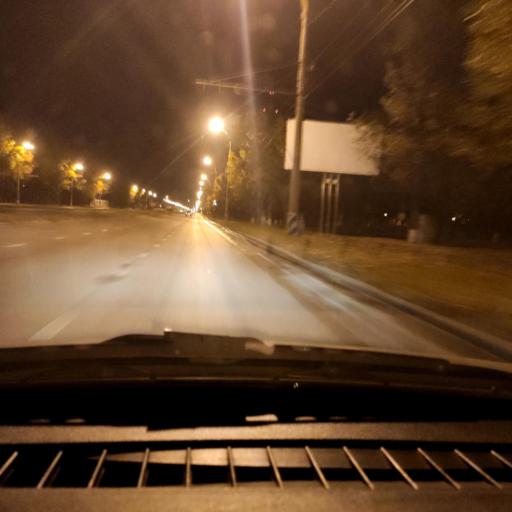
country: RU
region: Samara
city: Tol'yatti
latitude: 53.5254
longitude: 49.2607
